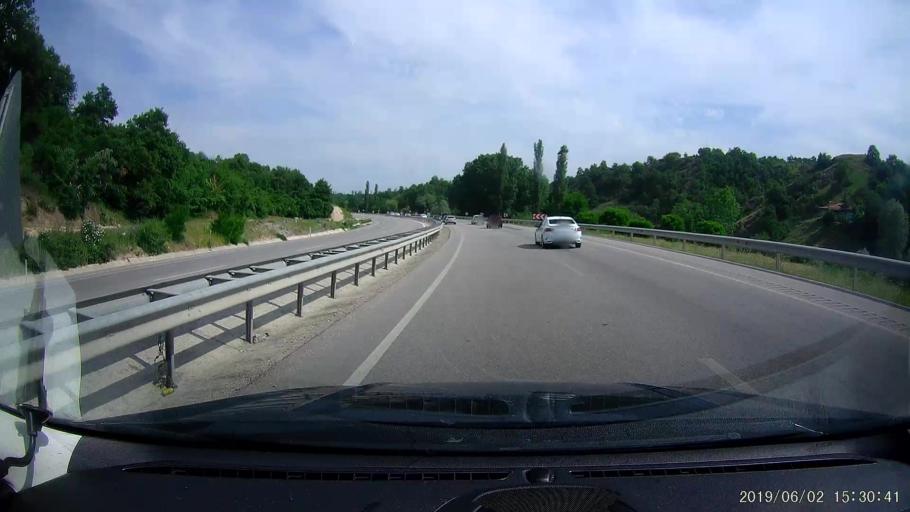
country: TR
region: Amasya
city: Saraycik
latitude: 40.9511
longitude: 35.1138
